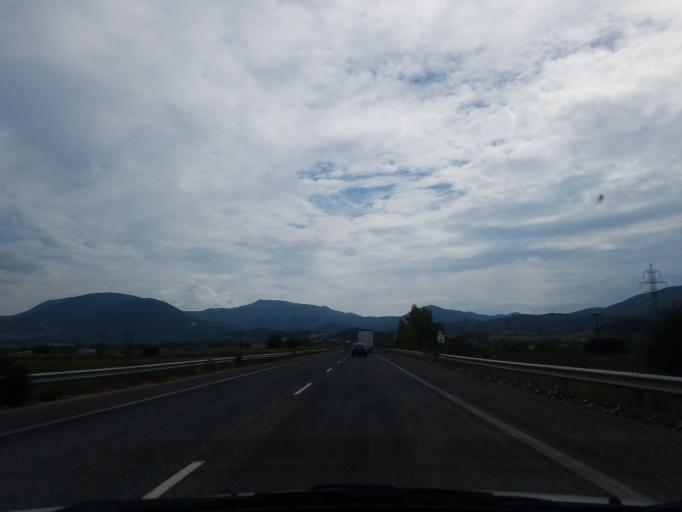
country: GR
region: Central Greece
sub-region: Nomos Fthiotidos
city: Domokos
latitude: 39.0385
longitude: 22.3567
